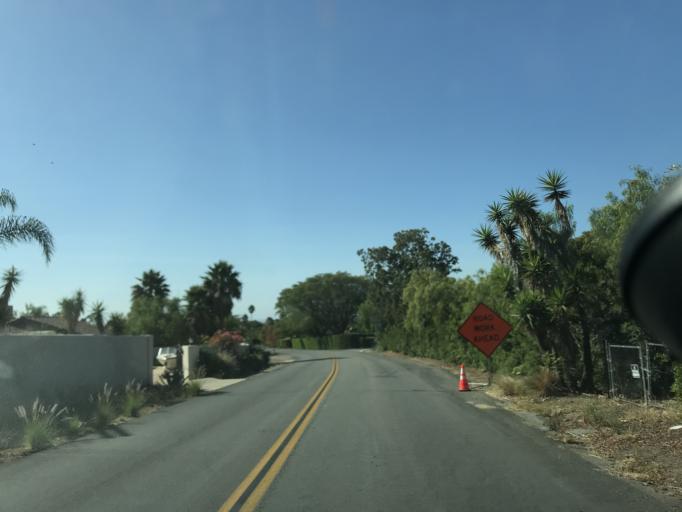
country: US
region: California
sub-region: Santa Barbara County
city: Goleta
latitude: 34.4659
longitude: -119.7772
